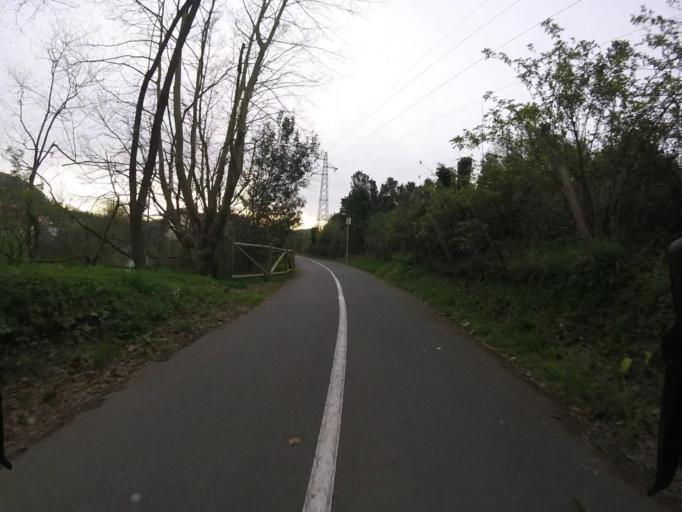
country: ES
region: Basque Country
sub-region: Provincia de Guipuzcoa
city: Lezo
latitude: 43.2943
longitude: -1.8556
